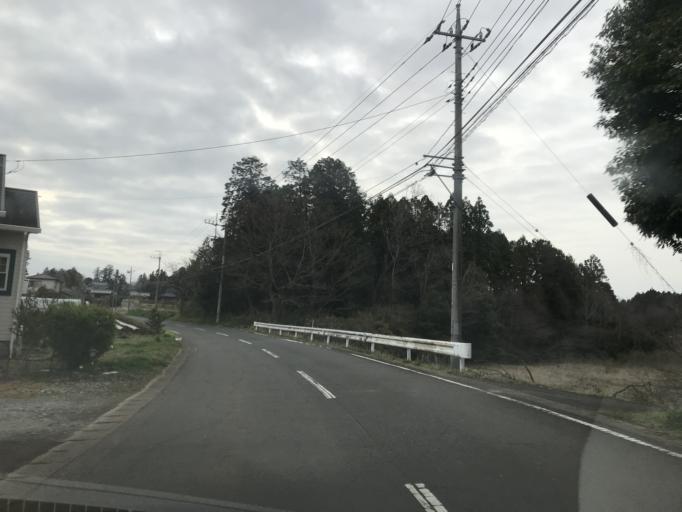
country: JP
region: Chiba
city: Sawara
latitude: 35.8115
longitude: 140.5375
